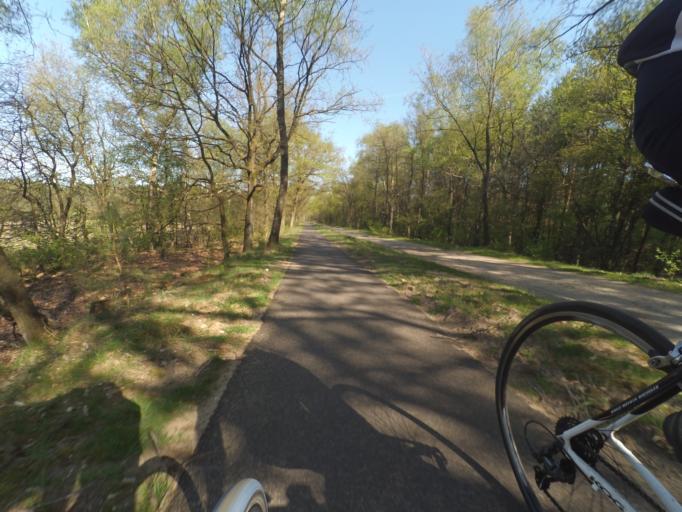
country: NL
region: Gelderland
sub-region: Gemeente Apeldoorn
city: Uddel
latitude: 52.1891
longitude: 5.8066
